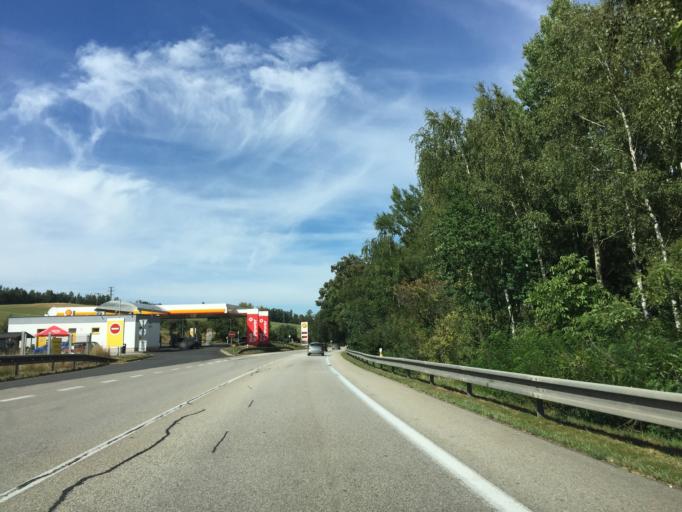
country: CZ
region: Central Bohemia
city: Votice
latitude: 49.6543
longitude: 14.6329
